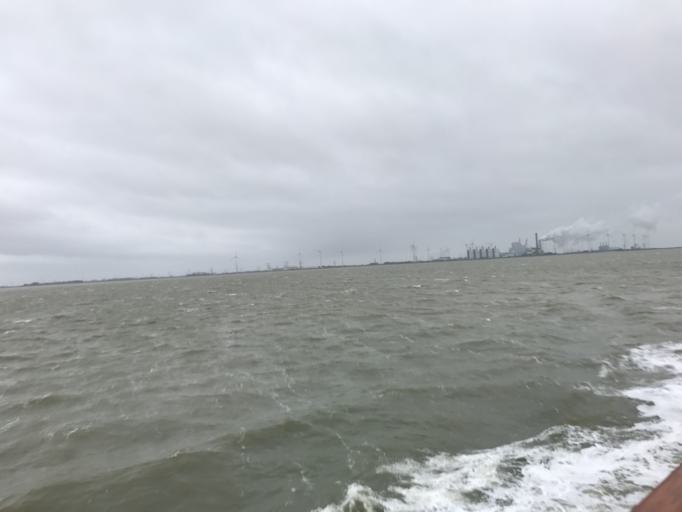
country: NL
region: Groningen
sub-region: Gemeente Delfzijl
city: Delfzijl
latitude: 53.4243
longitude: 6.9243
